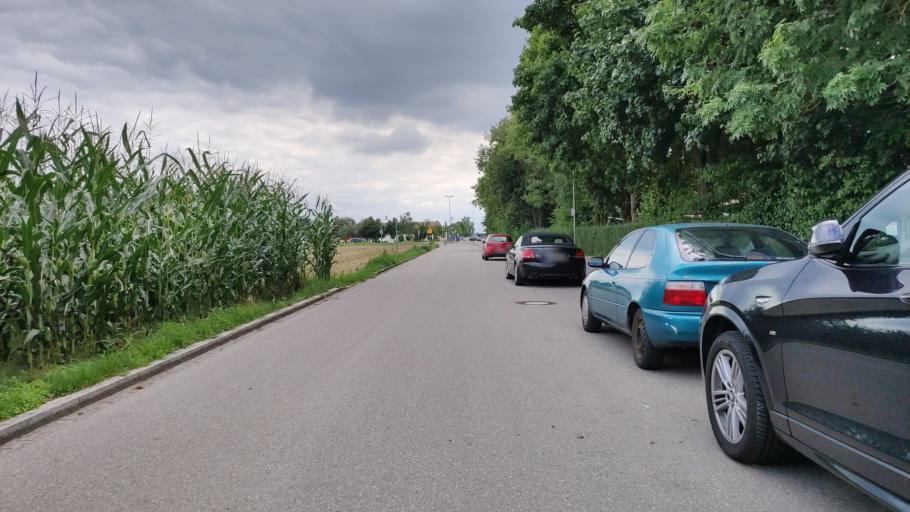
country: DE
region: Bavaria
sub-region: Swabia
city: Konigsbrunn
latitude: 48.2582
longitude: 10.8745
